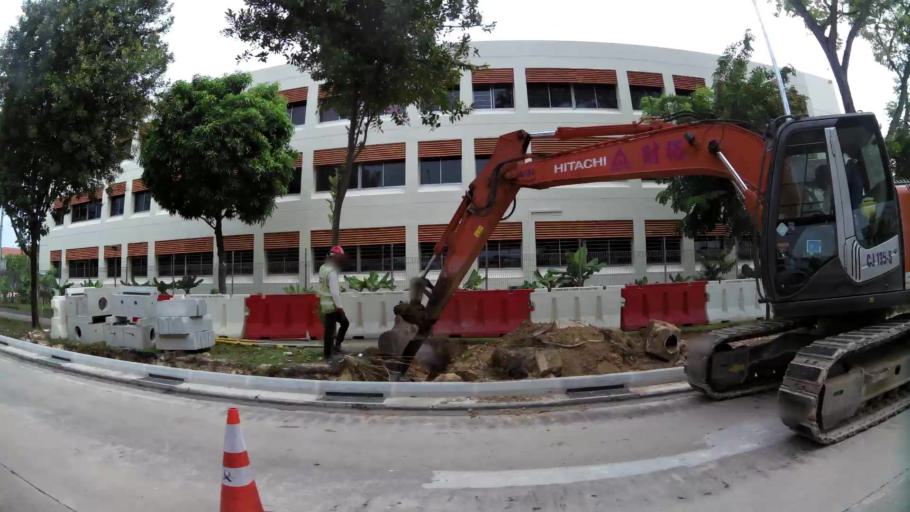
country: SG
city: Singapore
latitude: 1.3111
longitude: 103.7561
